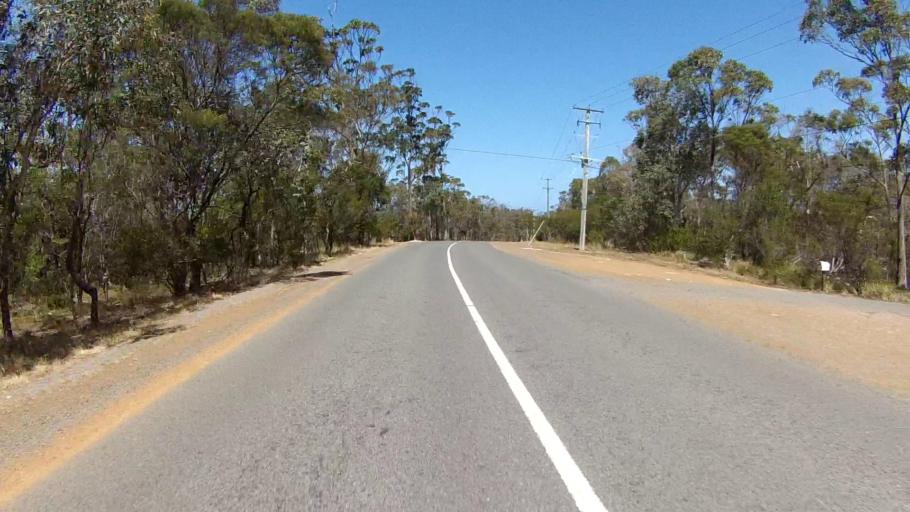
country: AU
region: Tasmania
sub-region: Clarence
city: Sandford
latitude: -43.0043
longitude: 147.4782
